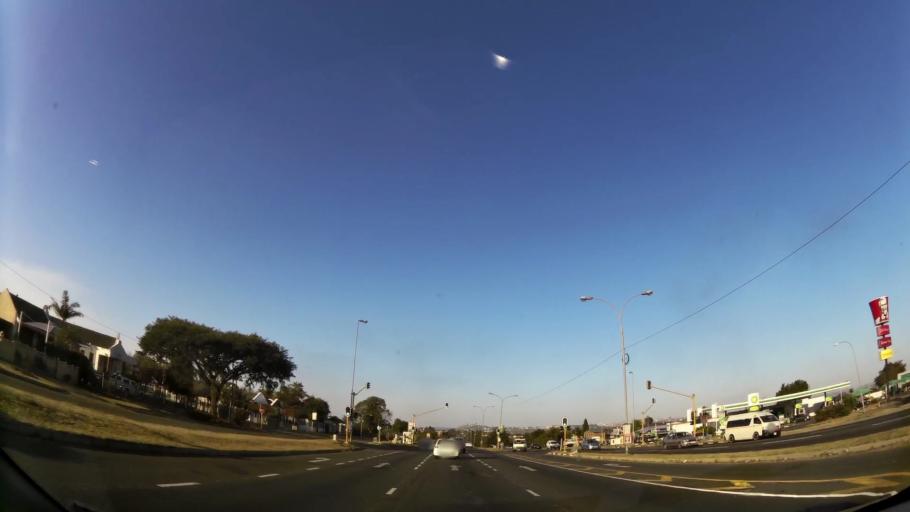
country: ZA
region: Gauteng
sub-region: City of Johannesburg Metropolitan Municipality
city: Roodepoort
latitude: -26.1473
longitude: 27.8920
